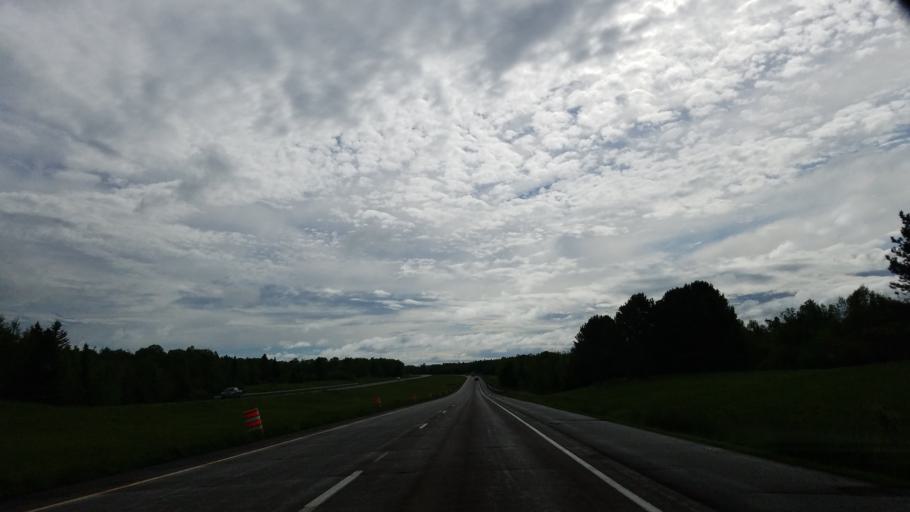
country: US
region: Minnesota
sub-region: Lake County
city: Two Harbors
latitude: 46.9291
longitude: -91.8411
